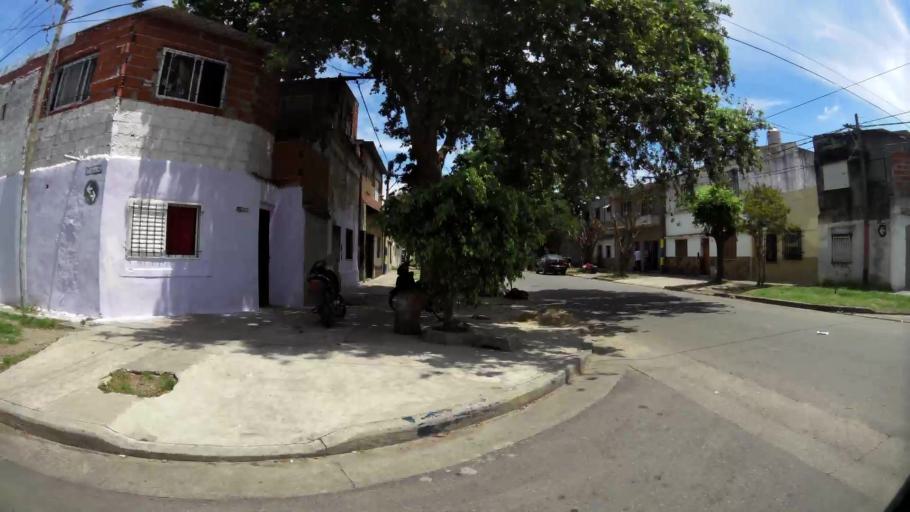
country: AR
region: Santa Fe
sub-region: Departamento de Rosario
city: Rosario
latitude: -32.9829
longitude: -60.6320
